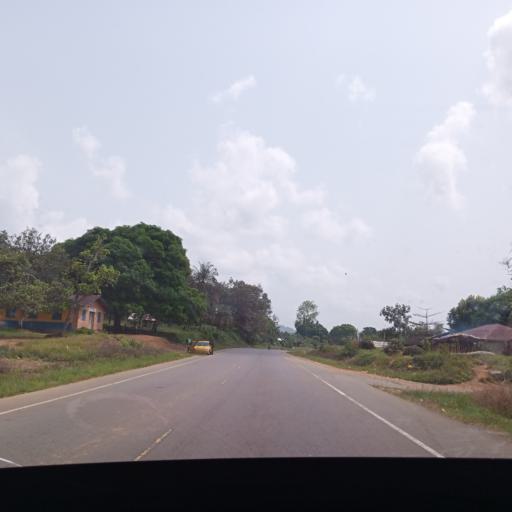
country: LR
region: Margibi
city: Kakata
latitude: 6.2505
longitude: -10.2974
